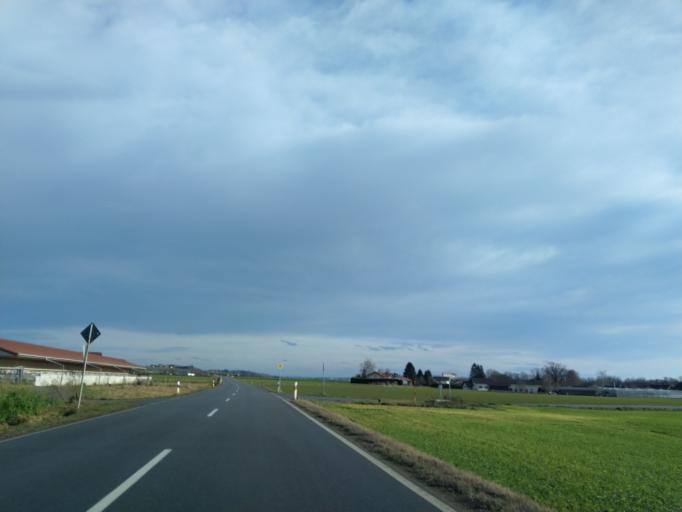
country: DE
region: Bavaria
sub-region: Lower Bavaria
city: Aldersbach
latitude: 48.6121
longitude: 13.0418
